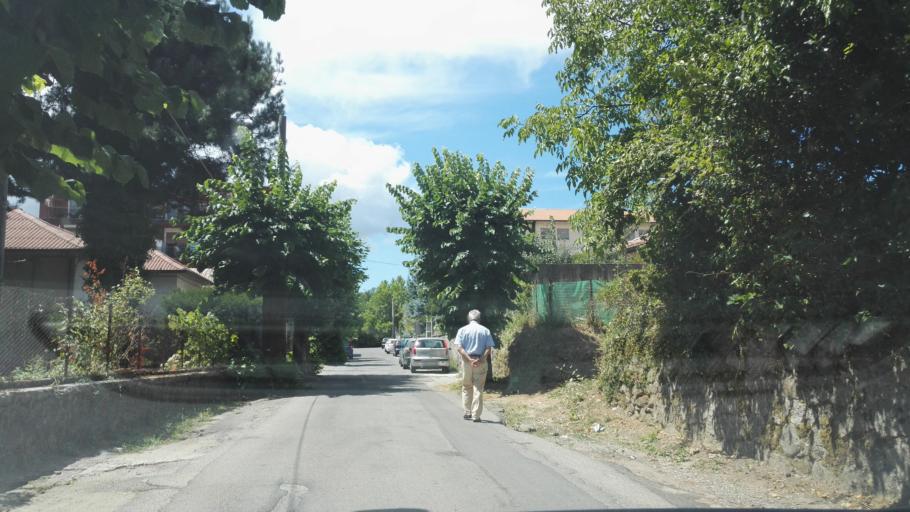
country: IT
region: Calabria
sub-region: Provincia di Vibo-Valentia
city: Serra San Bruno
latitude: 38.5788
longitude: 16.3263
